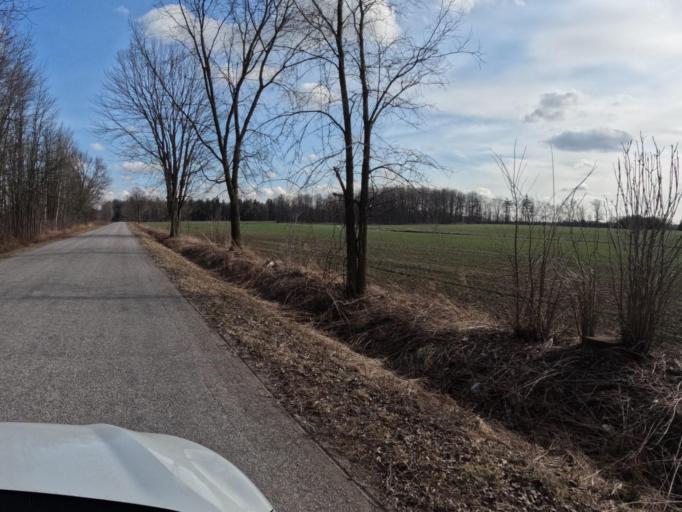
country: CA
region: Ontario
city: Brant
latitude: 42.9981
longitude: -80.4112
